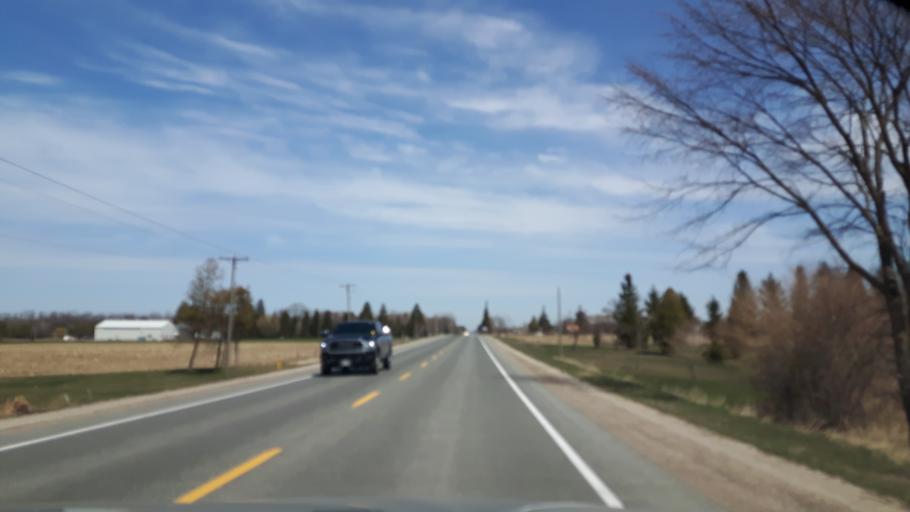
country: CA
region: Ontario
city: Goderich
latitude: 43.6929
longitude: -81.7056
